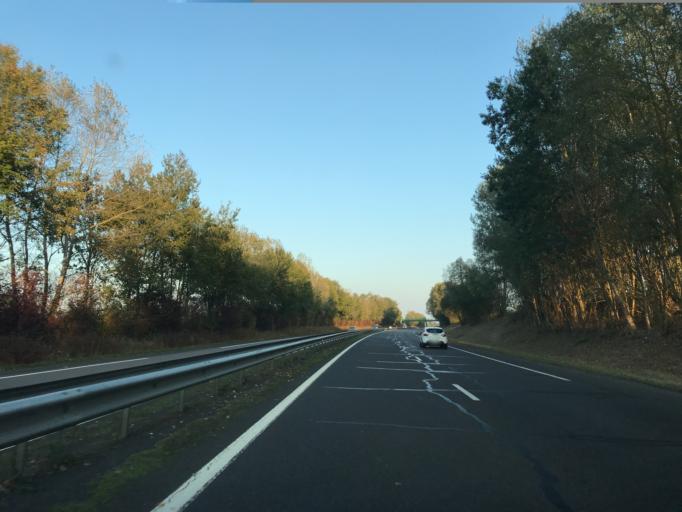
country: FR
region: Lower Normandy
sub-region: Departement de l'Orne
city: Mortagne-au-Perche
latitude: 48.5106
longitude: 0.3991
